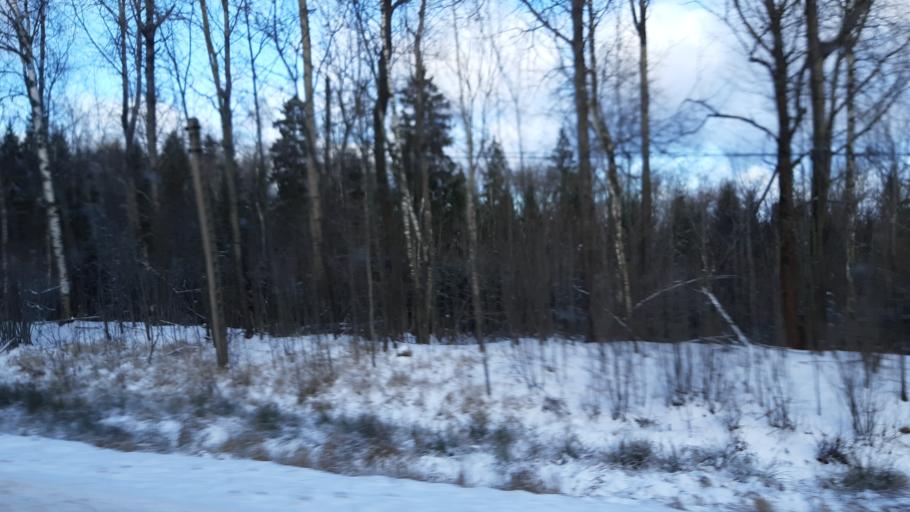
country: RU
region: Moskovskaya
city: Svatkovo
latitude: 56.3160
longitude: 38.3052
